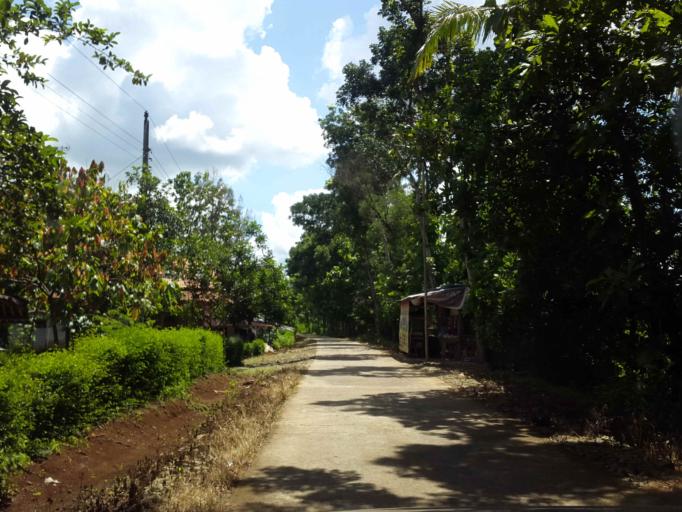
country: ID
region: Central Java
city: Jatiroto
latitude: -7.8149
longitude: 111.0310
